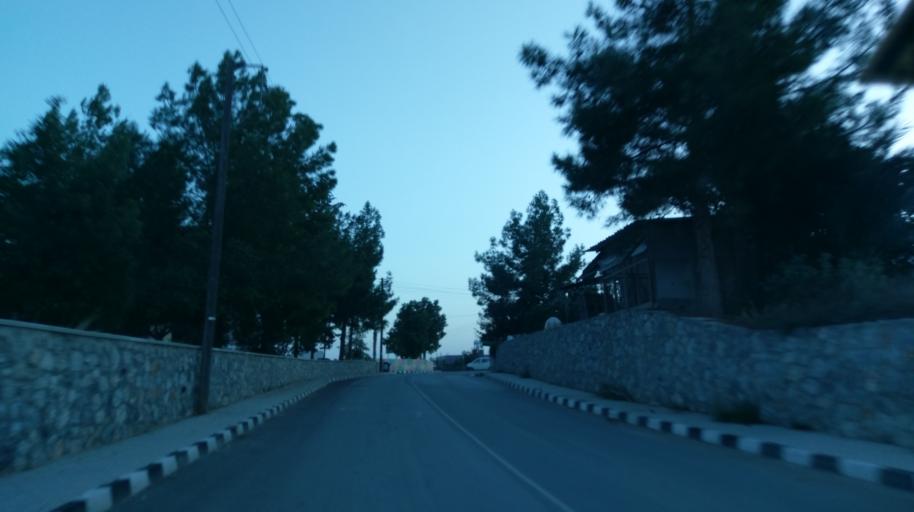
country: CY
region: Ammochostos
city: Trikomo
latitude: 35.2898
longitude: 33.8915
